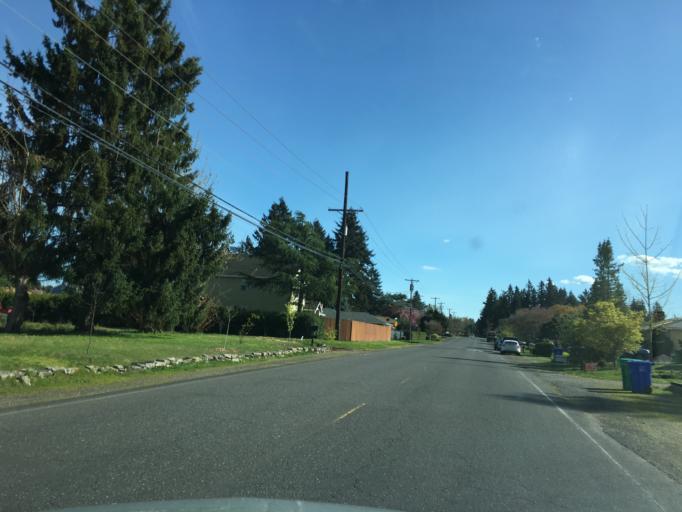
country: US
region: Oregon
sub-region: Multnomah County
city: Lents
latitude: 45.5405
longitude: -122.5271
